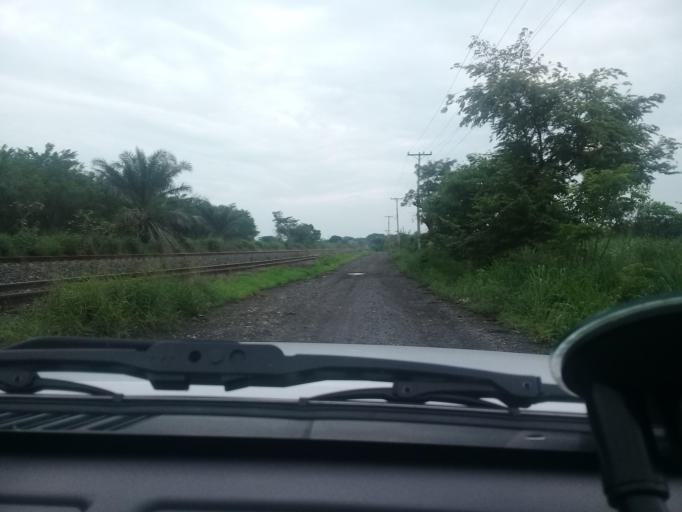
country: MX
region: Veracruz
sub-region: Puente Nacional
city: Cabezas
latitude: 19.3687
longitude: -96.3895
